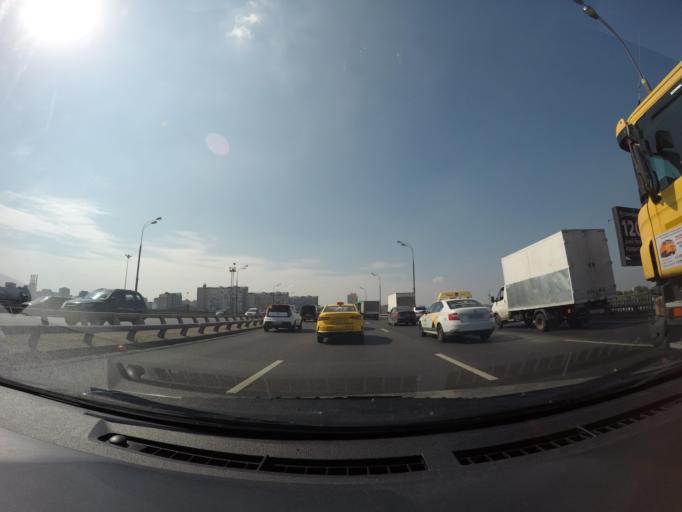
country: RU
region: Moscow
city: Sokol'niki
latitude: 55.7937
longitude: 37.6461
